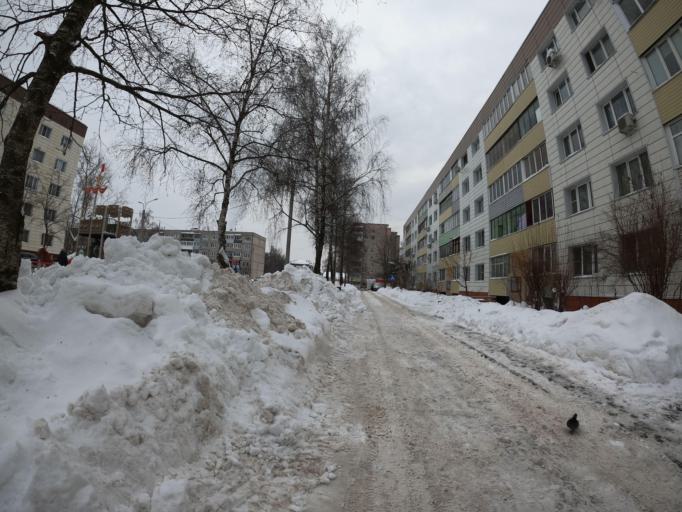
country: RU
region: Moskovskaya
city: Elektrogorsk
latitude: 55.8690
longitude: 38.7816
